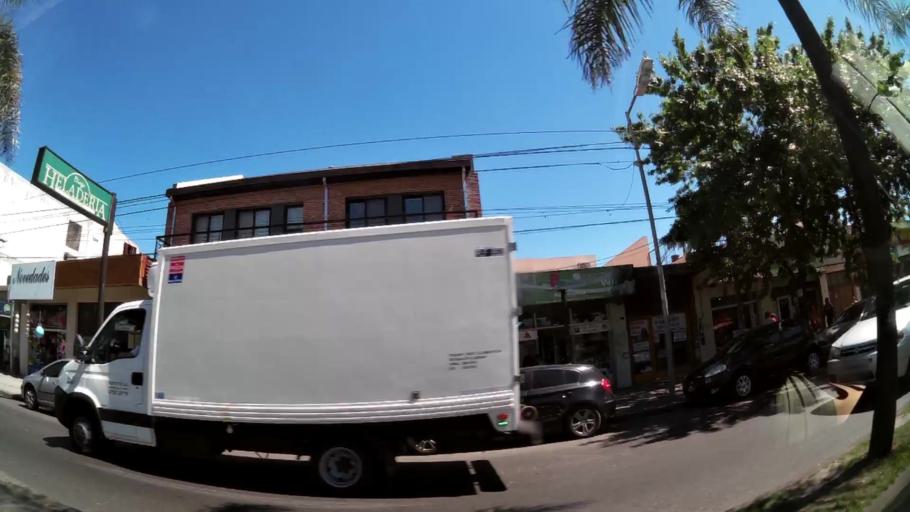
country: AR
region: Buenos Aires
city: Hurlingham
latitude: -34.4995
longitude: -58.6416
